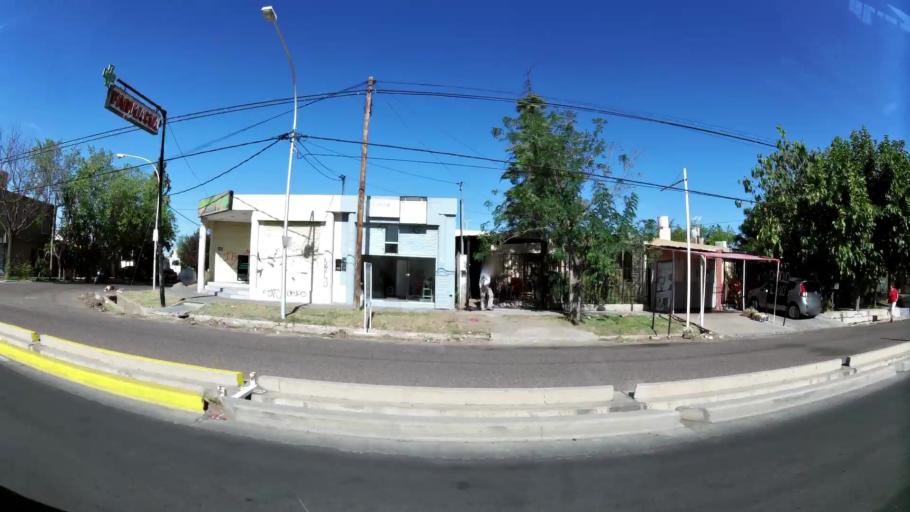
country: AR
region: Mendoza
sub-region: Departamento de Godoy Cruz
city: Godoy Cruz
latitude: -32.9355
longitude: -68.8004
